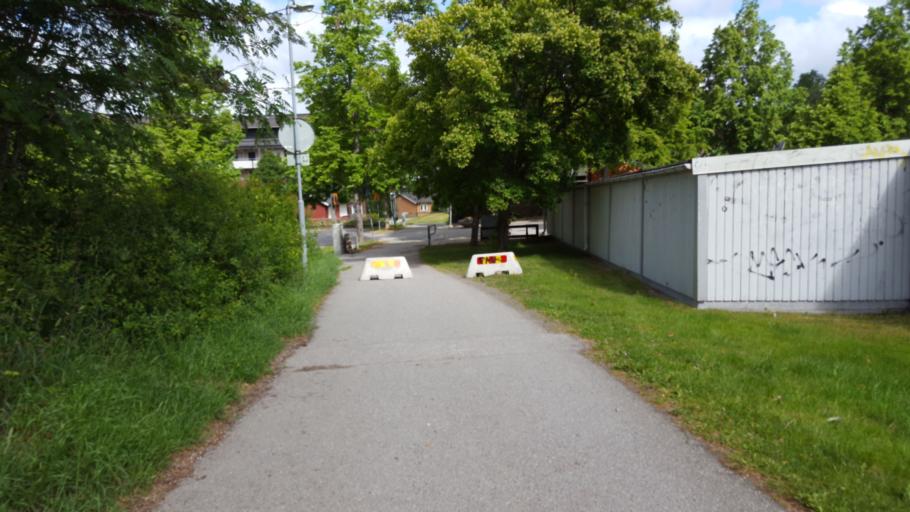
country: SE
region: Stockholm
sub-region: Upplands Vasby Kommun
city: Upplands Vaesby
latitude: 59.5114
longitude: 17.8835
